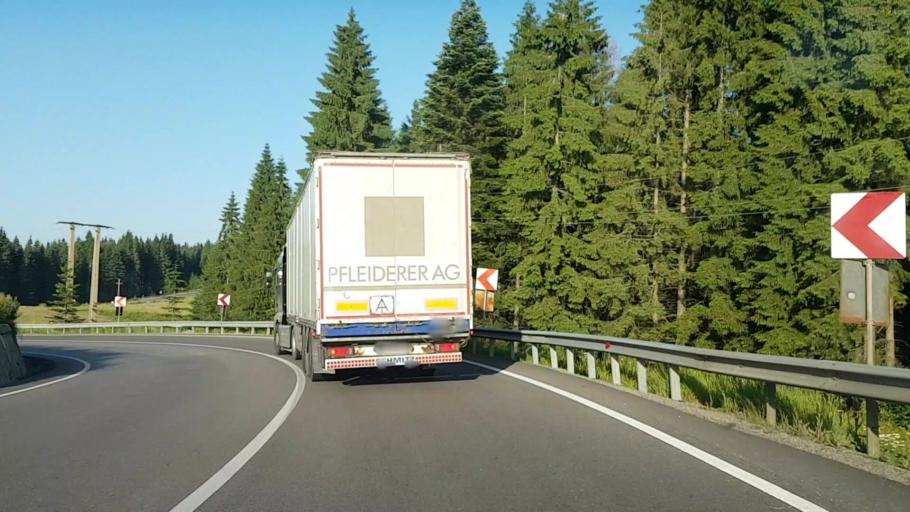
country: RO
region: Suceava
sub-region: Comuna Poiana Stampei
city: Poiana Stampei
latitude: 47.2859
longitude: 25.0614
